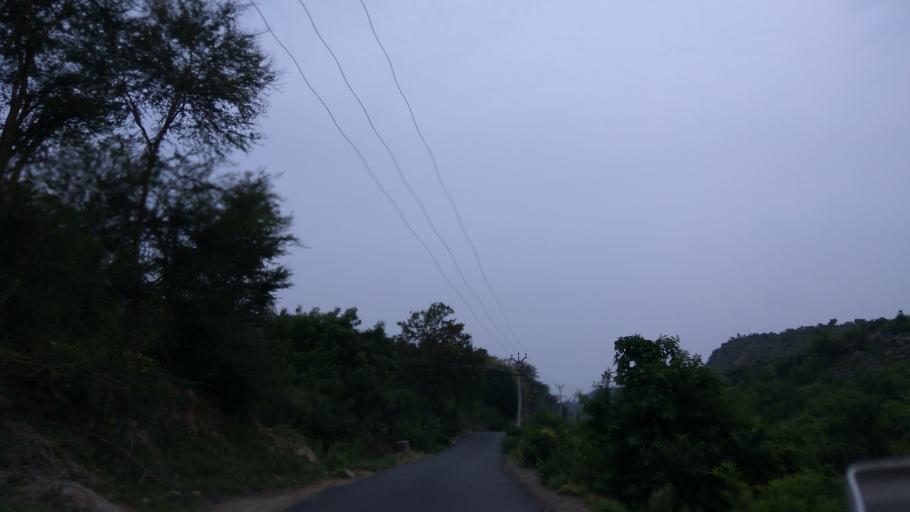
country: IN
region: Tamil Nadu
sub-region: Dharmapuri
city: Dharmapuri
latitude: 12.0189
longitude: 78.1219
